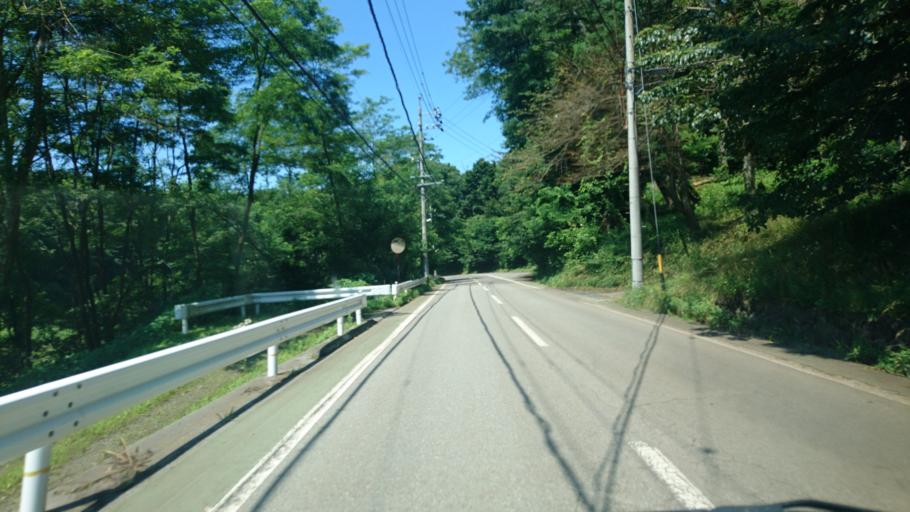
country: JP
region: Nagano
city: Saku
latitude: 36.3237
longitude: 138.5794
